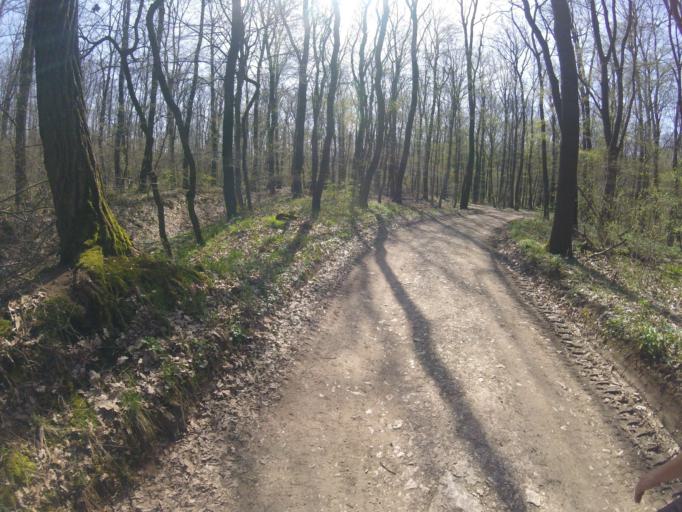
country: HU
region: Pest
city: Pilisszanto
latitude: 47.6533
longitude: 18.8654
